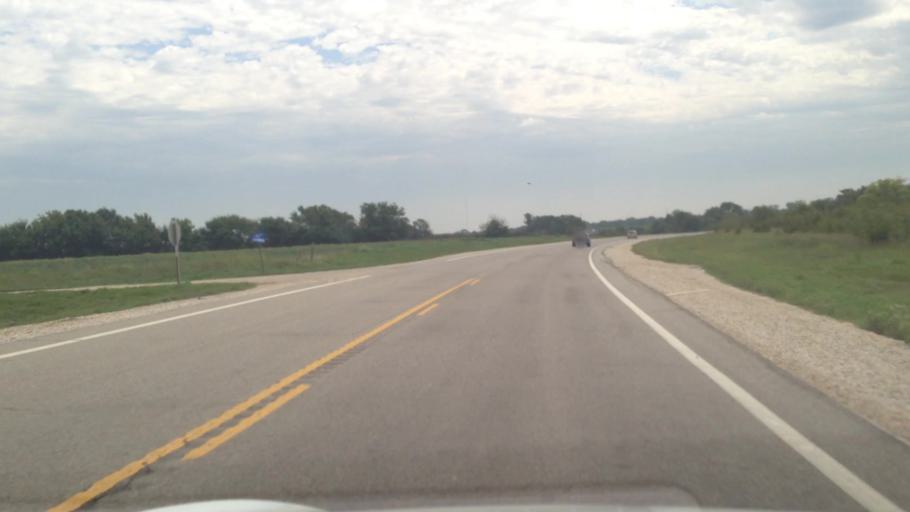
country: US
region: Kansas
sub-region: Allen County
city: Iola
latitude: 37.9207
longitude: -95.1593
